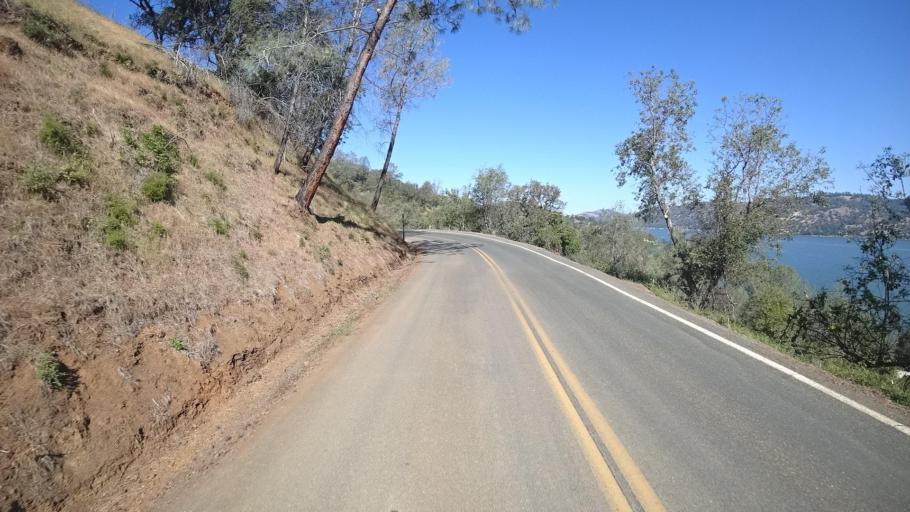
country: US
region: California
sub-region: Lake County
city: Clearlake Oaks
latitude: 38.9967
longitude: -122.6935
